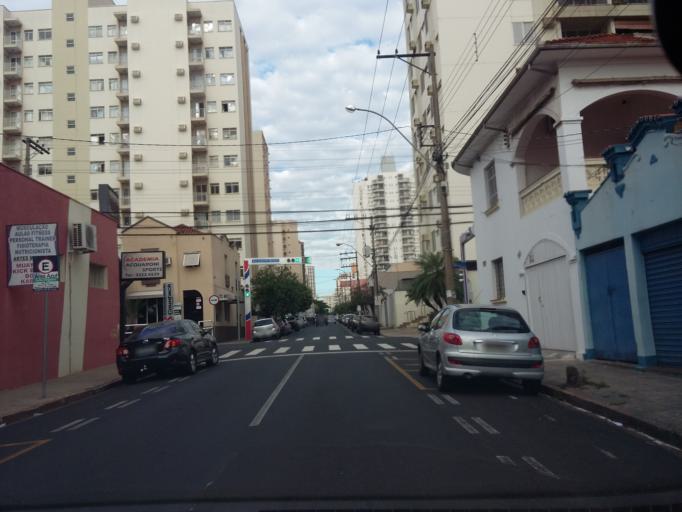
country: BR
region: Sao Paulo
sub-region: Sao Jose Do Rio Preto
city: Sao Jose do Rio Preto
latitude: -20.8124
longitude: -49.3861
